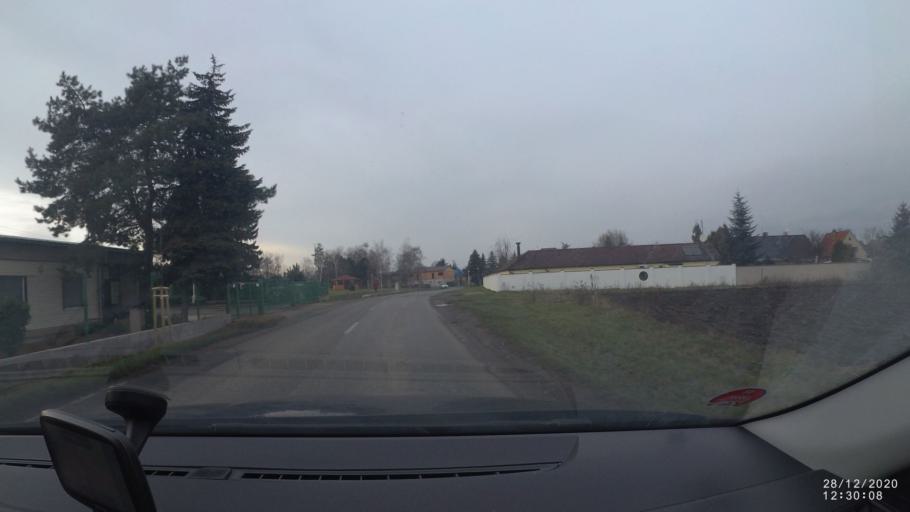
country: CZ
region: Central Bohemia
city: Kostelec nad Labem
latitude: 50.1998
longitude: 14.6014
